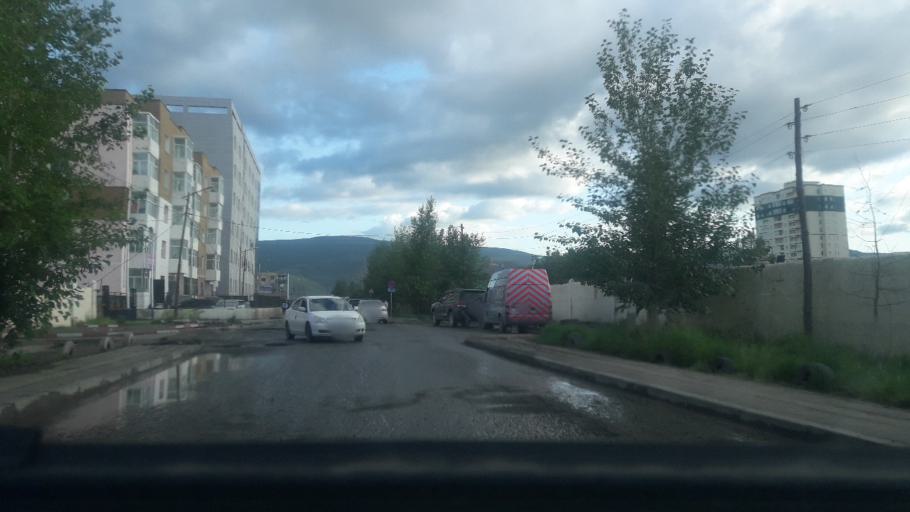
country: MN
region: Ulaanbaatar
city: Ulaanbaatar
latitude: 47.9162
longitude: 106.9945
